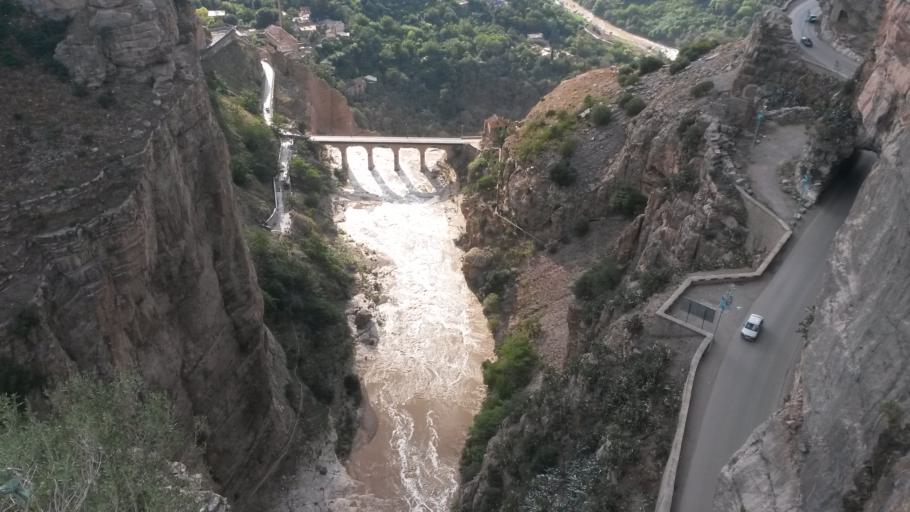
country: DZ
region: Constantine
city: Constantine
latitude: 36.3727
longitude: 6.6152
